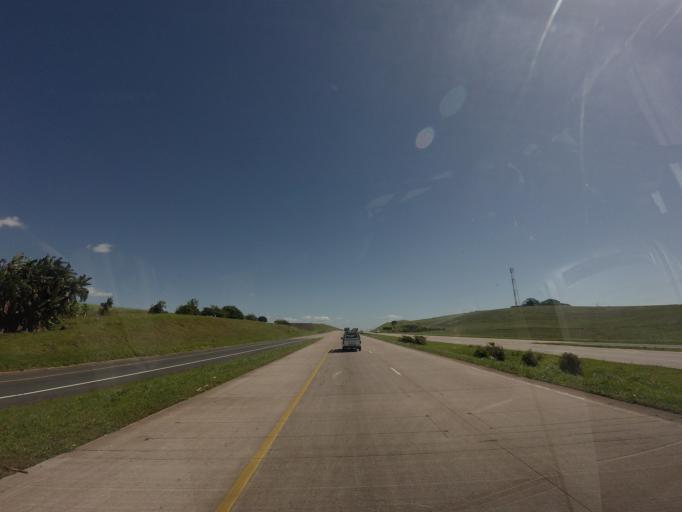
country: ZA
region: KwaZulu-Natal
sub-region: iLembe District Municipality
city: Stanger
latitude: -29.4252
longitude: 31.2734
